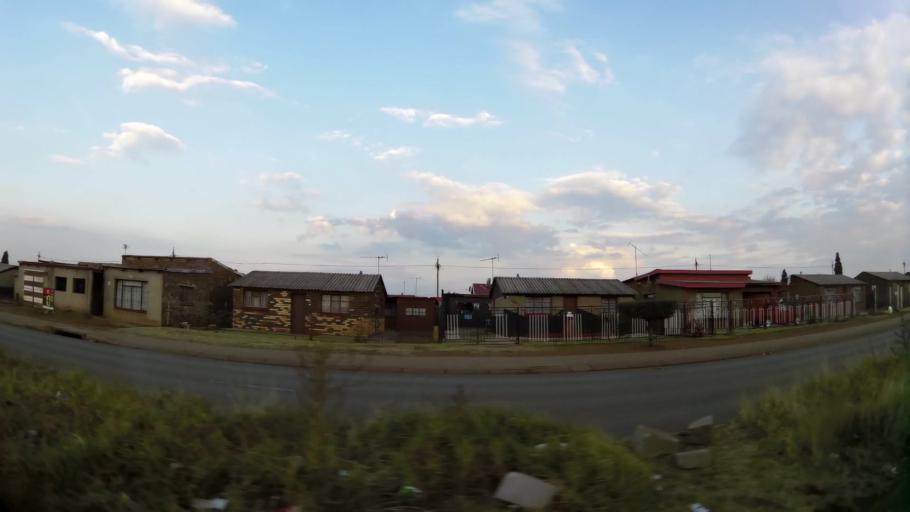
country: ZA
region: Gauteng
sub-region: City of Johannesburg Metropolitan Municipality
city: Orange Farm
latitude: -26.5677
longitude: 27.8481
